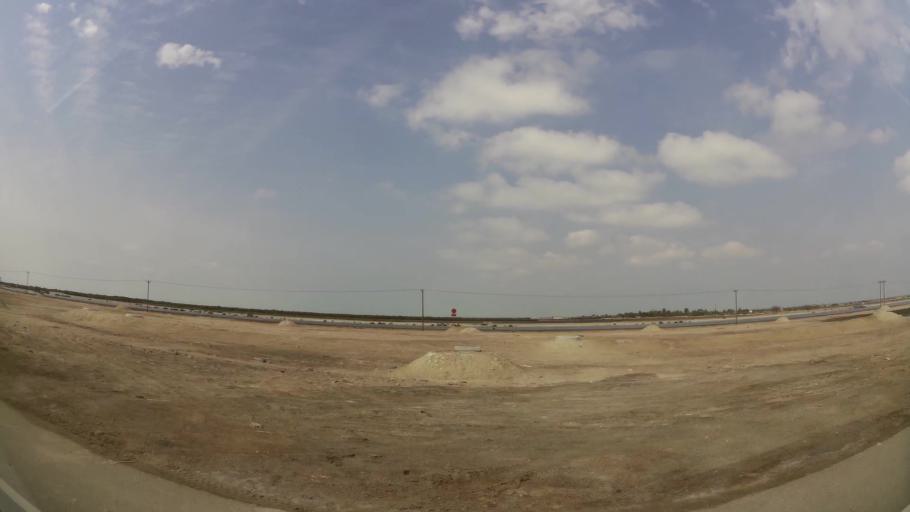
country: AE
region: Abu Dhabi
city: Abu Dhabi
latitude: 24.5750
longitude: 54.6427
